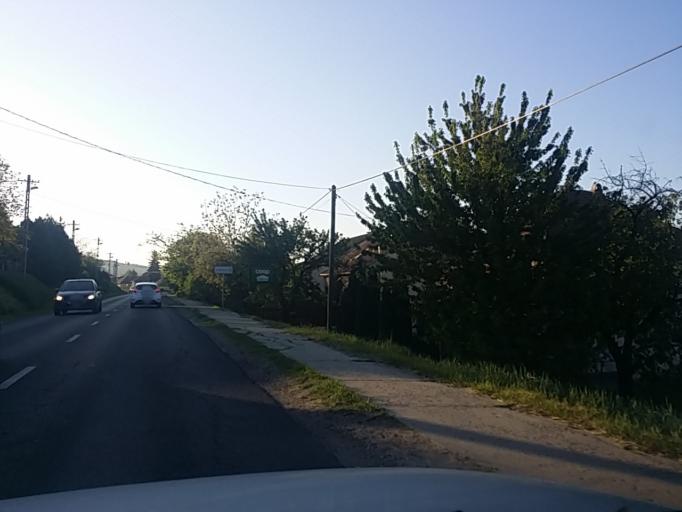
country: HU
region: Pest
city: Mogyorod
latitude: 47.5969
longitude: 19.2297
